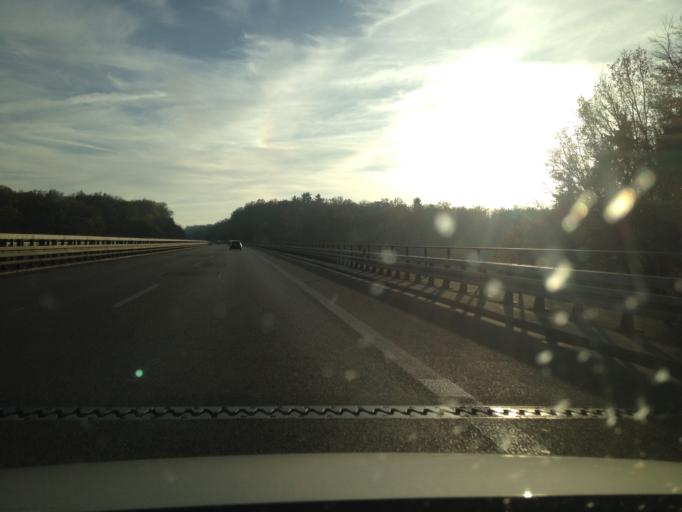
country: DE
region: Baden-Wuerttemberg
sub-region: Tuebingen Region
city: Nerenstetten
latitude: 48.5361
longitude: 10.0914
